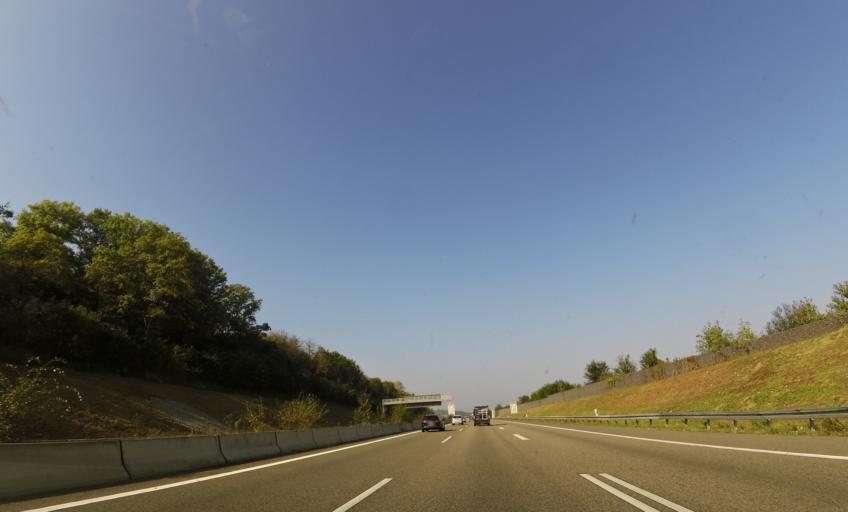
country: DE
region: Baden-Wuerttemberg
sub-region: Regierungsbezirk Stuttgart
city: Erlenbach
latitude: 49.1631
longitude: 9.2765
